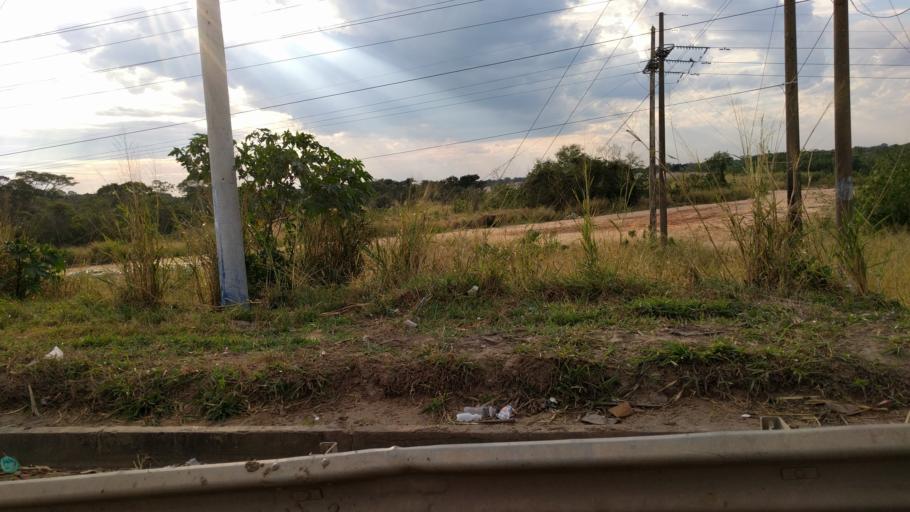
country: BO
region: Santa Cruz
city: Portachuelo
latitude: -17.3249
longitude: -63.3286
